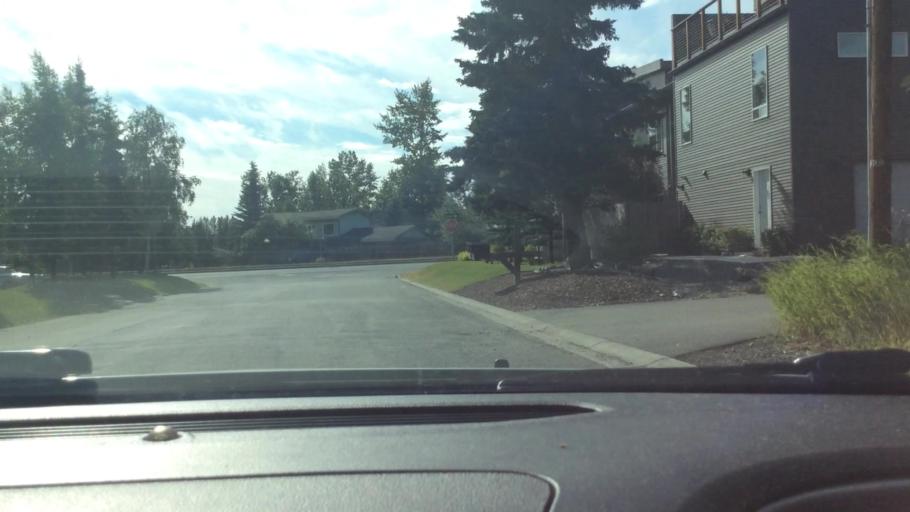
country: US
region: Alaska
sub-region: Anchorage Municipality
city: Anchorage
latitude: 61.1973
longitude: -149.7769
